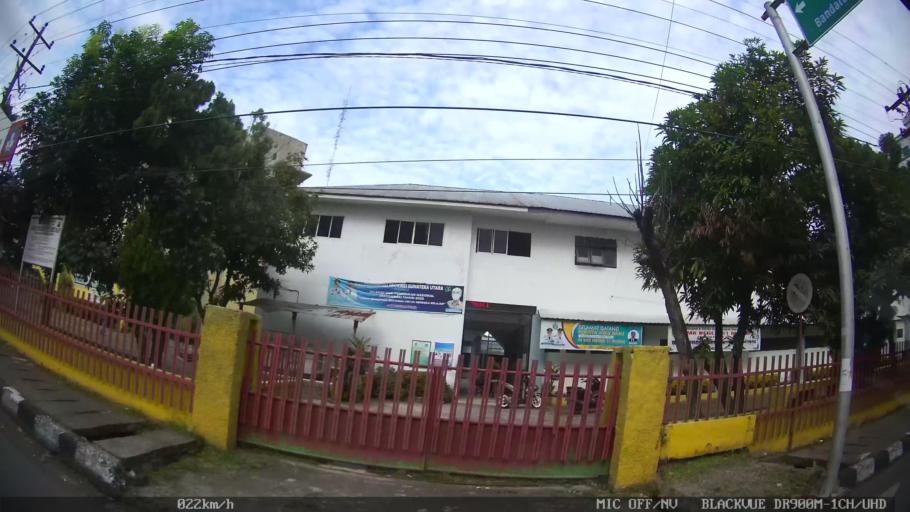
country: ID
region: North Sumatra
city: Medan
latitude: 3.5994
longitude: 98.6813
